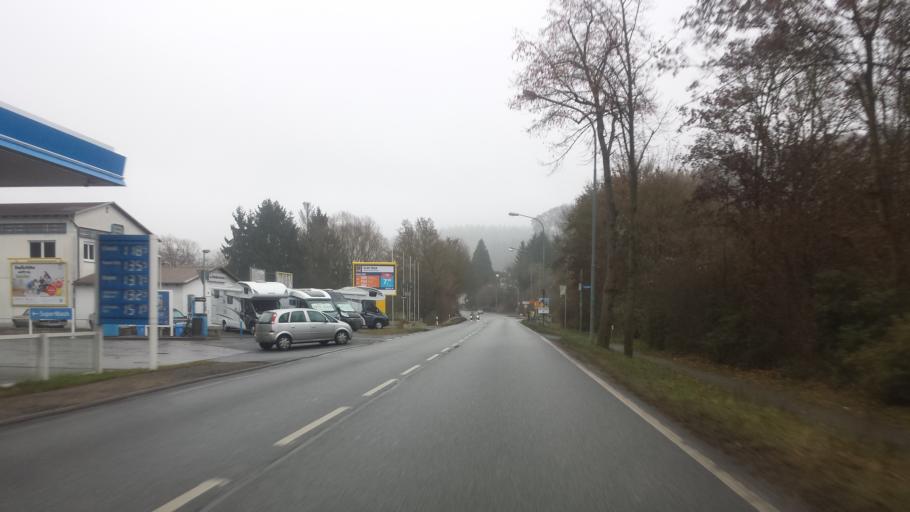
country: DE
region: Hesse
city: Ober-Ramstadt
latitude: 49.8301
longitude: 8.7057
